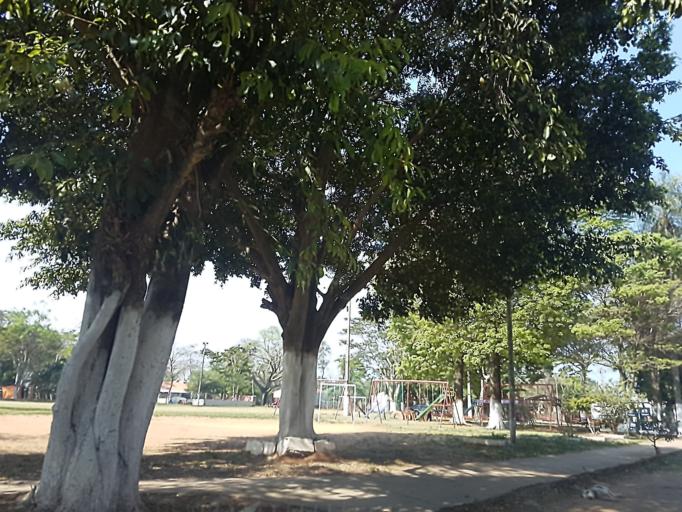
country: PY
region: Central
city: Colonia Mariano Roque Alonso
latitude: -25.2124
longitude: -57.5243
